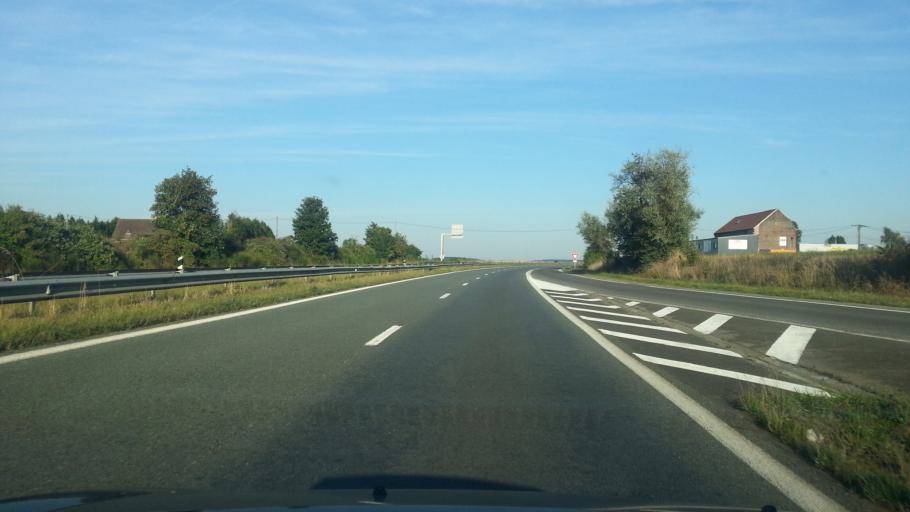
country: FR
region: Picardie
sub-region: Departement de l'Oise
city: Bresles
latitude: 49.4180
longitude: 2.2468
